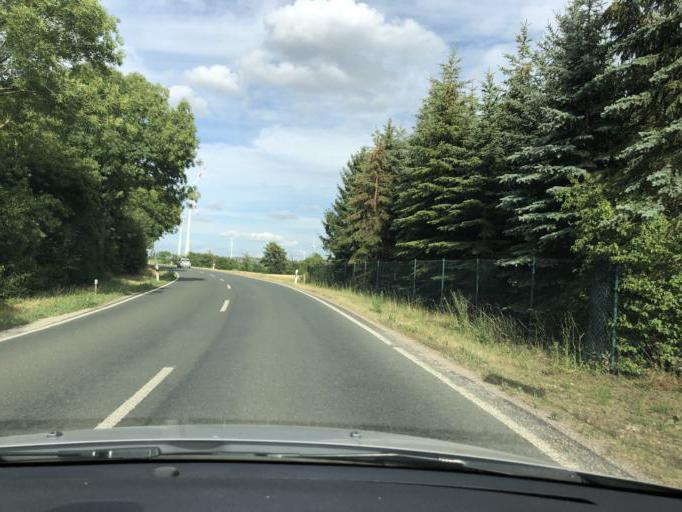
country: DE
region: Thuringia
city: Hainichen
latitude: 51.0316
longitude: 11.6043
